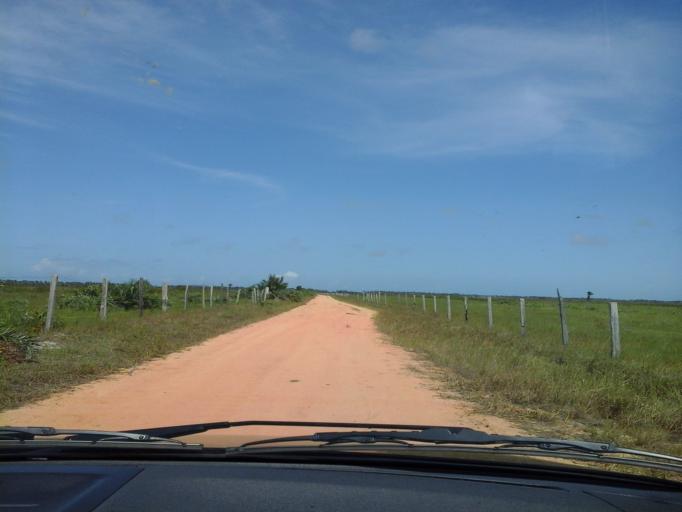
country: BR
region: Bahia
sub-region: Nova Vicosa
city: Nova Vicosa
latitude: -17.6819
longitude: -39.1640
